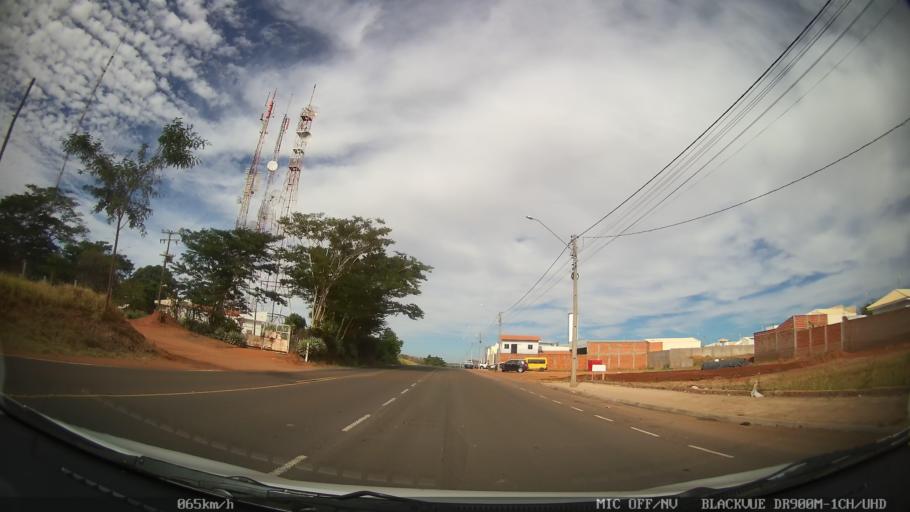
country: BR
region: Sao Paulo
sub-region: Catanduva
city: Catanduva
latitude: -21.1636
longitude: -48.9627
